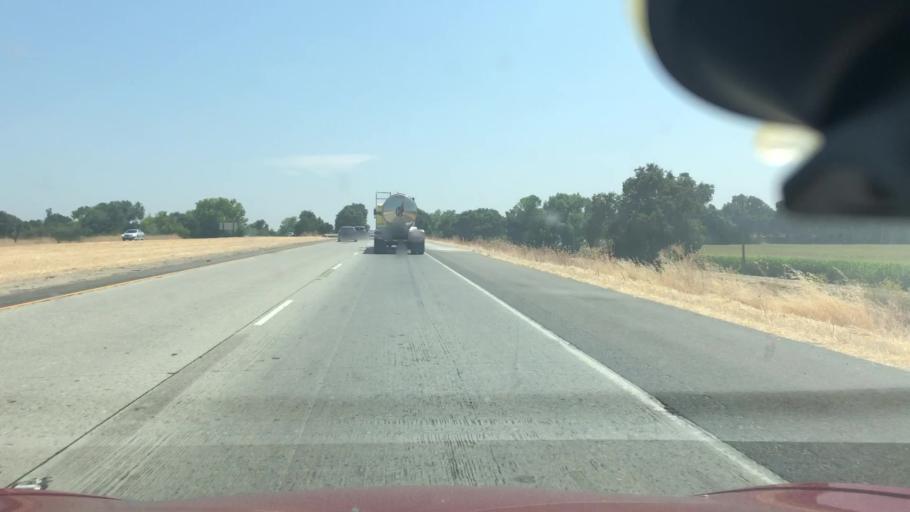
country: US
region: California
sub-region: San Joaquin County
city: Thornton
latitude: 38.2736
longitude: -121.4553
